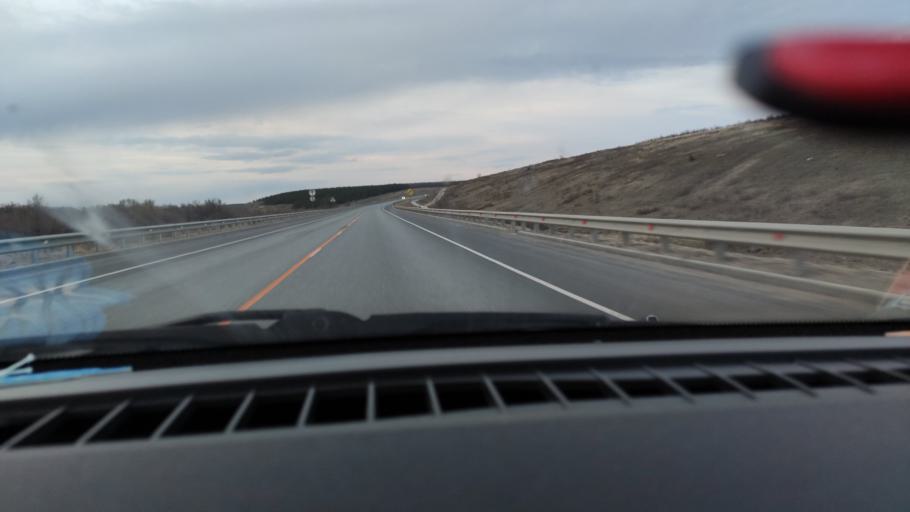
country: RU
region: Saratov
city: Yelshanka
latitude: 51.8737
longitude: 46.5057
